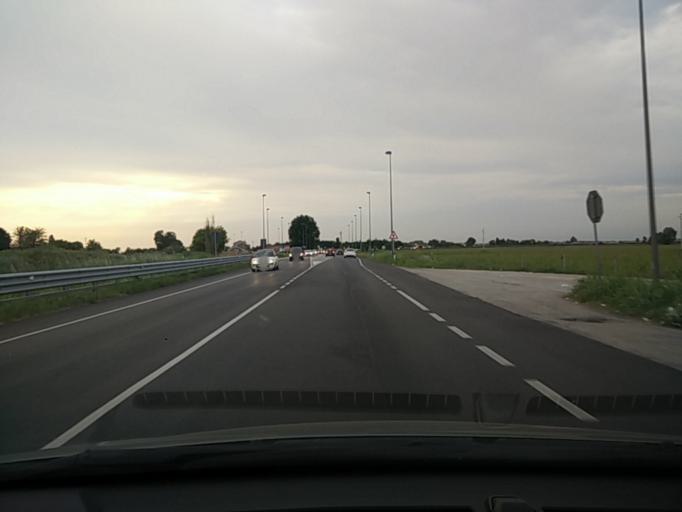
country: IT
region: Veneto
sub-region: Provincia di Venezia
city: Iesolo
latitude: 45.5452
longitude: 12.6111
